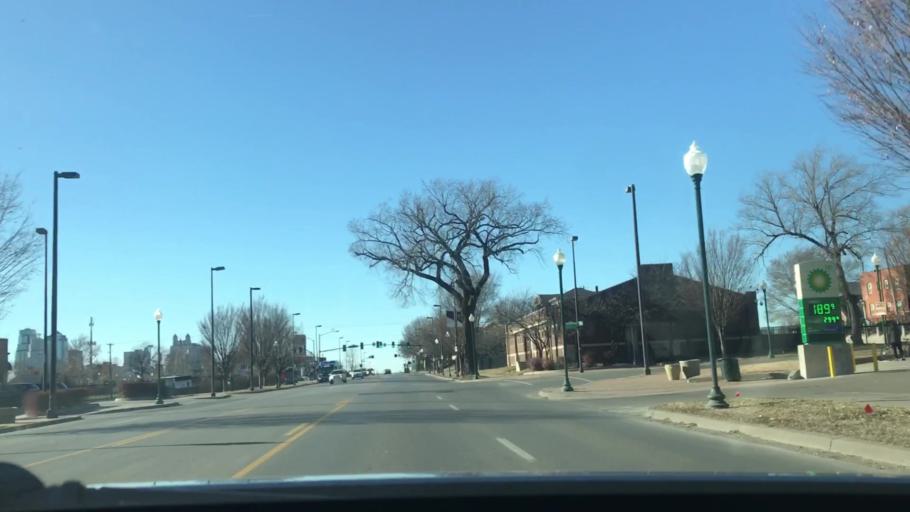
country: US
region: Missouri
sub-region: Jackson County
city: Kansas City
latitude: 39.1066
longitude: -94.5581
